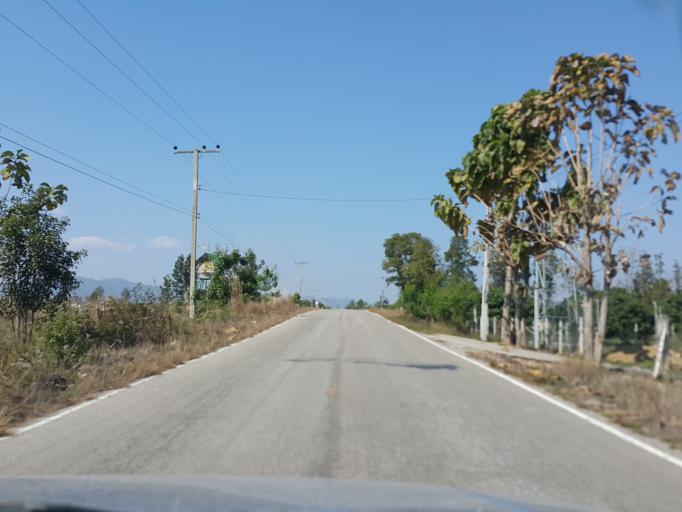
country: TH
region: Chiang Mai
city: Mae Wang
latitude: 18.5594
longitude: 98.7940
